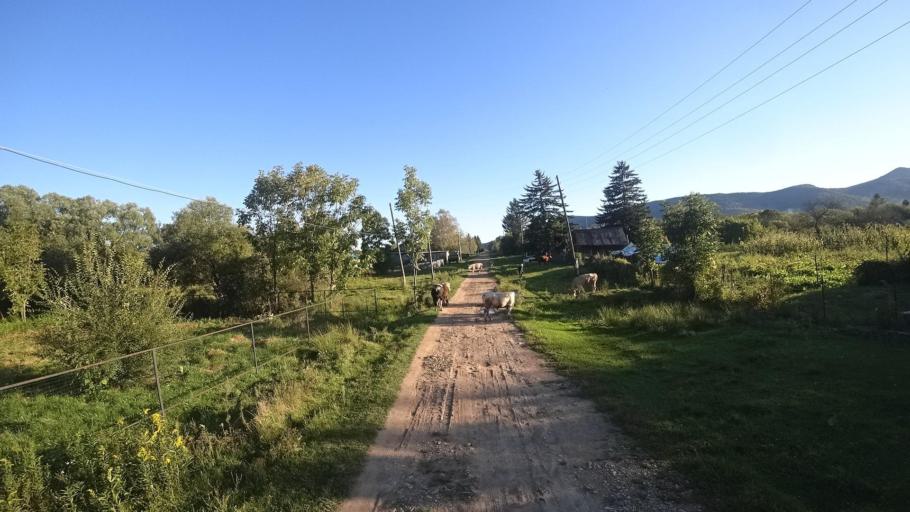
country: RU
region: Primorskiy
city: Kirovskiy
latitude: 44.8343
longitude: 133.5757
